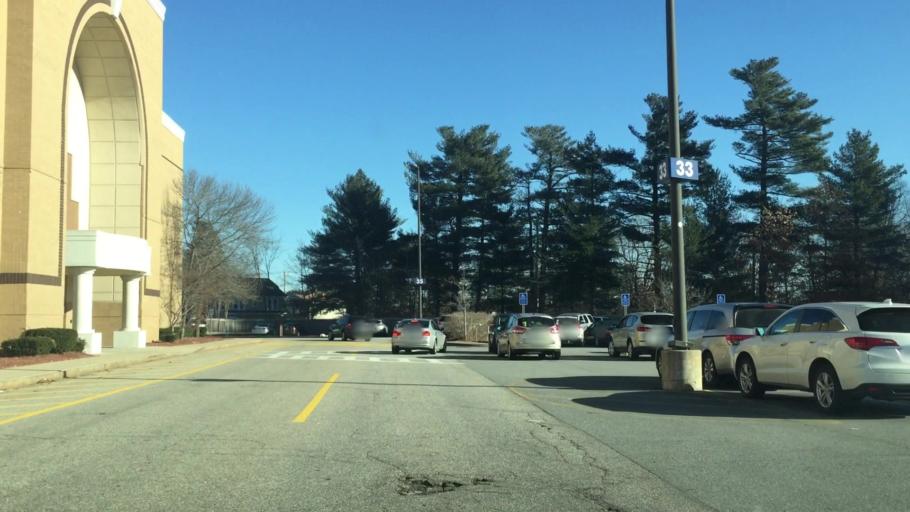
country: US
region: New Hampshire
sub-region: Hillsborough County
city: Manchester
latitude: 42.9548
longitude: -71.4310
